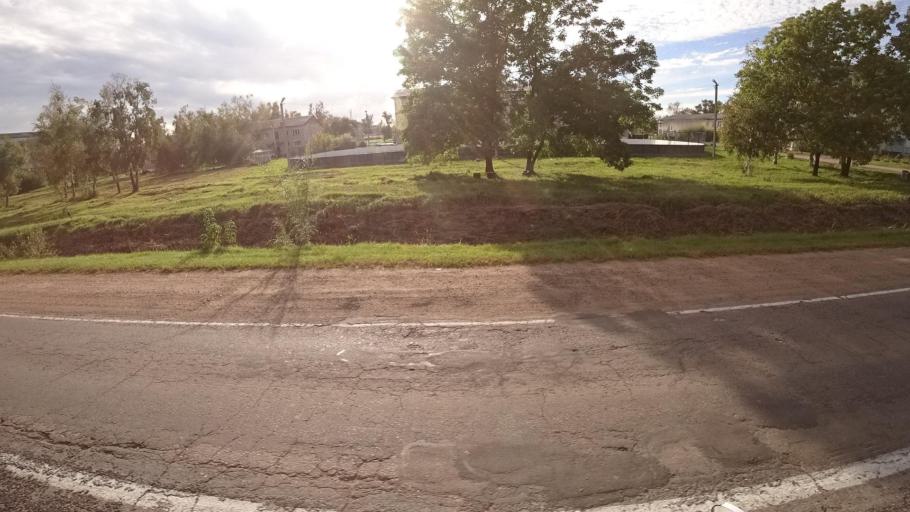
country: RU
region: Primorskiy
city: Dostoyevka
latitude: 44.2904
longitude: 133.4264
